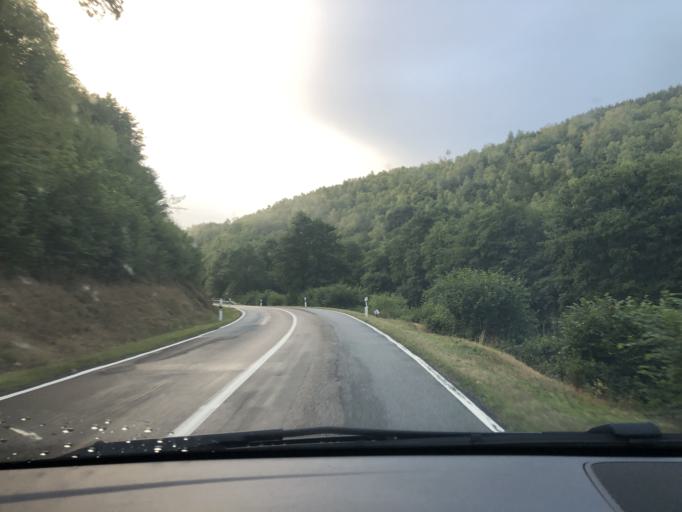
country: DE
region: Rheinland-Pfalz
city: Grimburg
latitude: 49.6001
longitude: 6.8782
